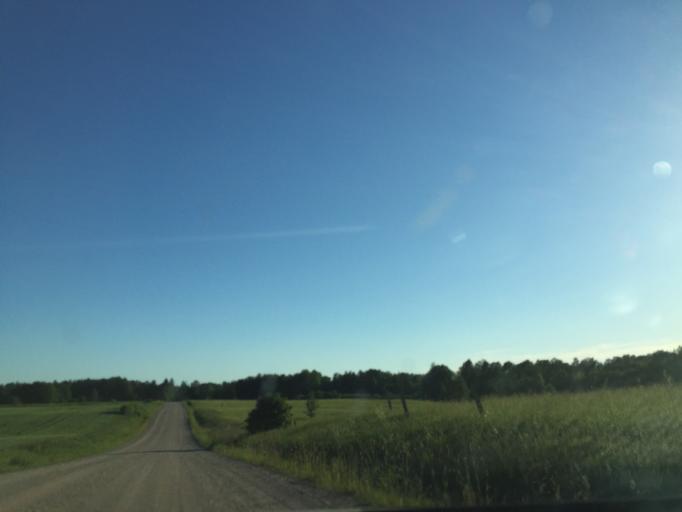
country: LV
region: Broceni
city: Broceni
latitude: 56.8295
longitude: 22.5601
